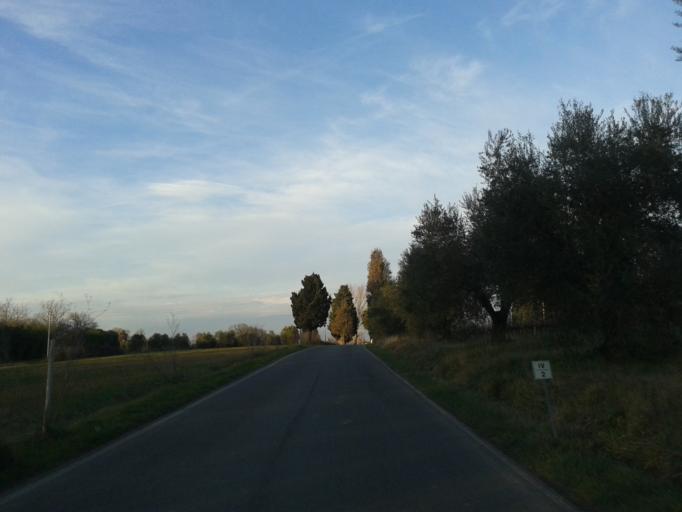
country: IT
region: Tuscany
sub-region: Provincia di Livorno
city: Collesalvetti
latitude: 43.5886
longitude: 10.4454
